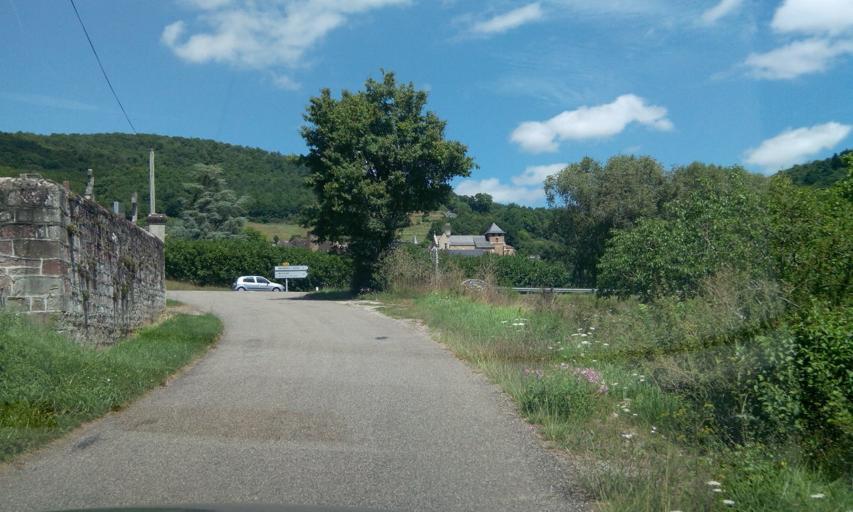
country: FR
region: Limousin
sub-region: Departement de la Correze
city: Meyssac
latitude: 45.0702
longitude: 1.6169
